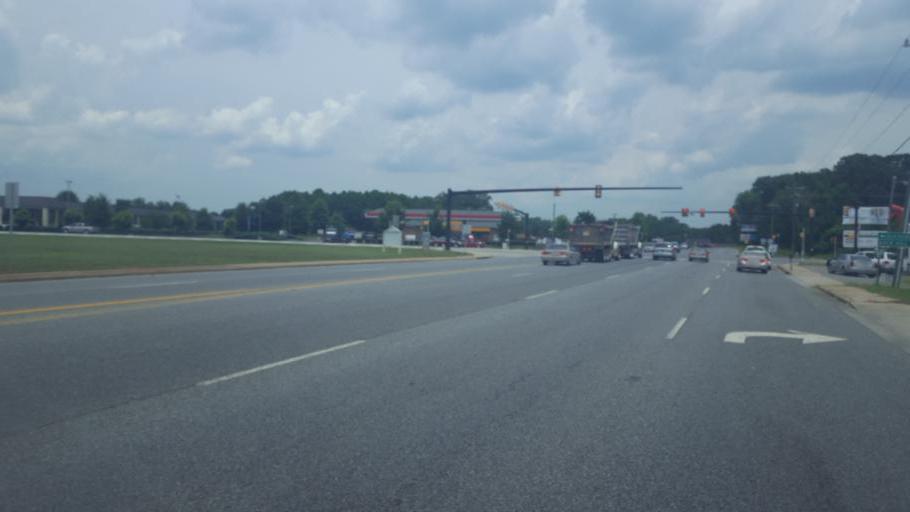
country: US
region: South Carolina
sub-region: York County
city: York
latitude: 34.9858
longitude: -81.2019
